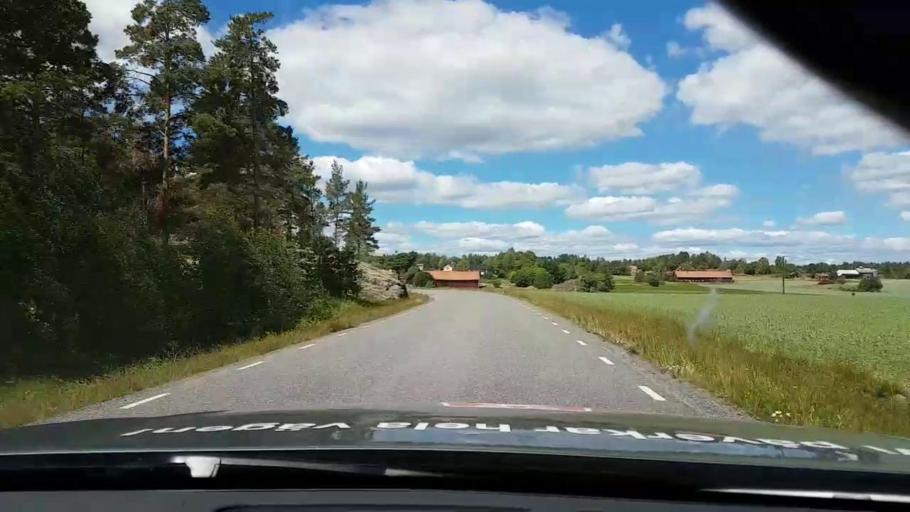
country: SE
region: Kalmar
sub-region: Vasterviks Kommun
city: Forserum
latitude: 58.0056
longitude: 16.5856
